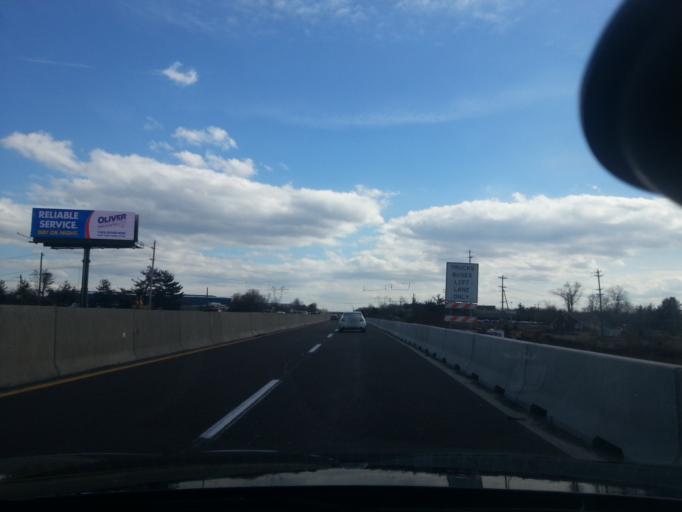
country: US
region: Pennsylvania
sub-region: Montgomery County
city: Kulpsville
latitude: 40.2608
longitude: -75.3522
